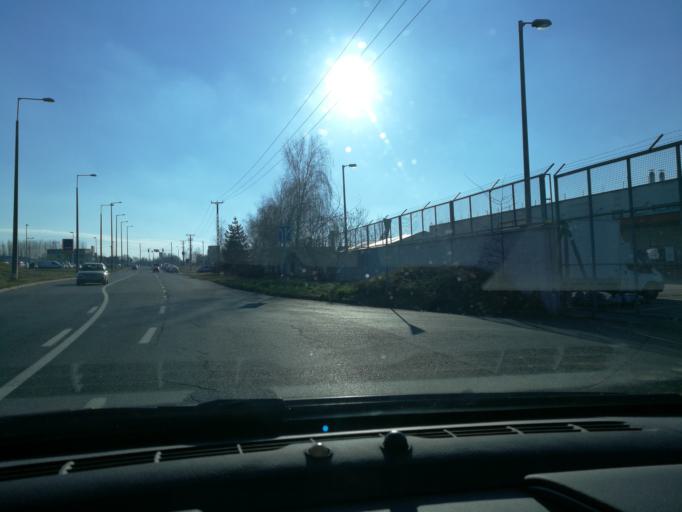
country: HU
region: Szabolcs-Szatmar-Bereg
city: Nyiregyhaza
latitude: 47.9722
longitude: 21.7398
